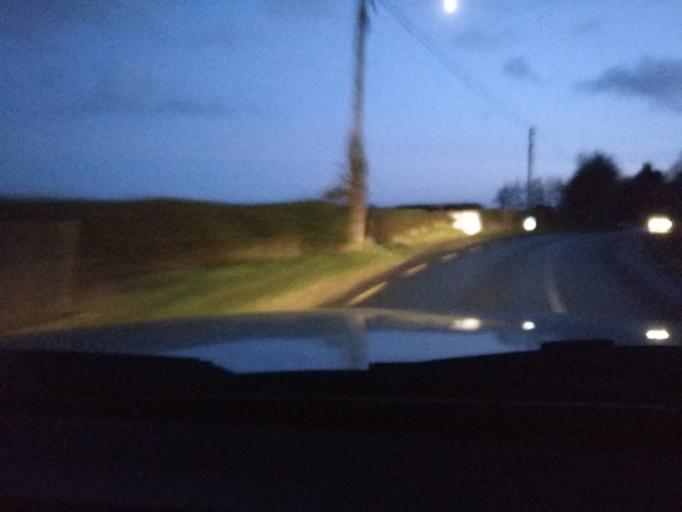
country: IE
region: Leinster
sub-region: Lu
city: Carlingford
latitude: 54.0548
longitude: -6.1960
